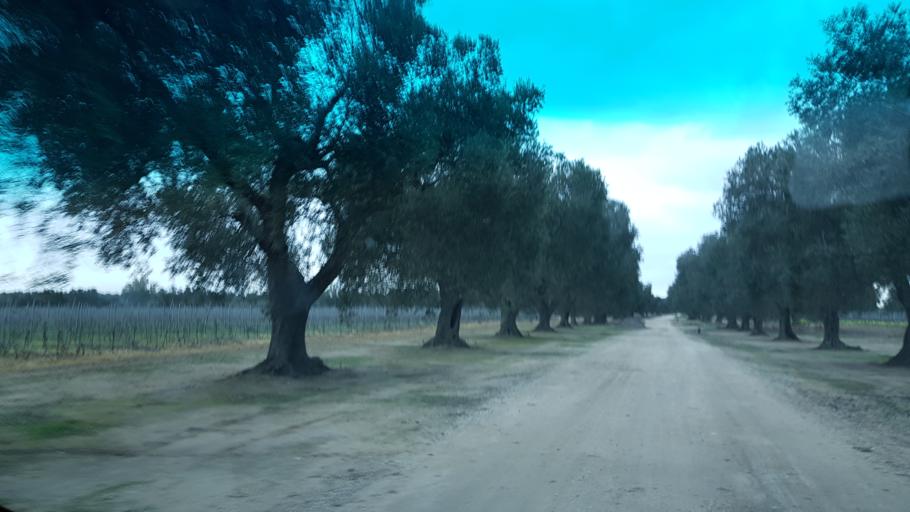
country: IT
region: Apulia
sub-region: Provincia di Brindisi
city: La Rosa
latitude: 40.5903
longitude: 17.9820
